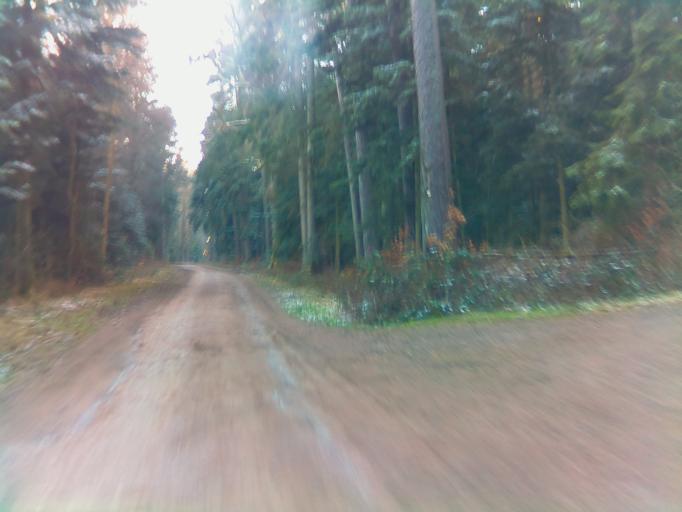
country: DE
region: Baden-Wuerttemberg
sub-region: Karlsruhe Region
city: Engelsbrand
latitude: 48.8129
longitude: 8.6600
